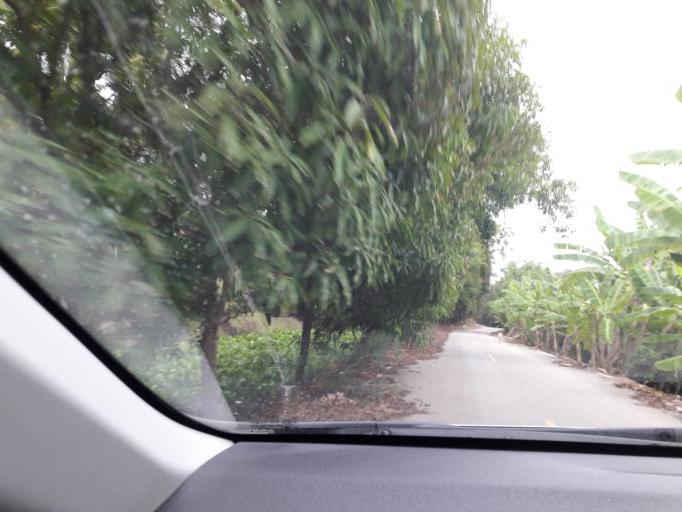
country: TH
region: Ratchaburi
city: Damnoen Saduak
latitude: 13.5487
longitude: 99.9725
